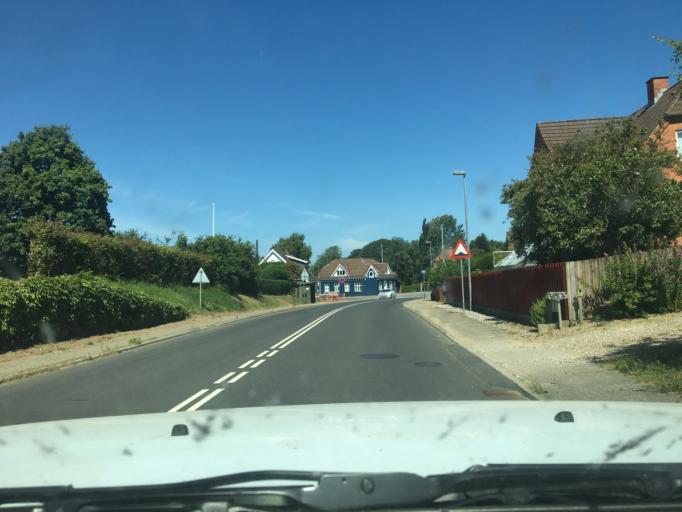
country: DK
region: Central Jutland
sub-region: Favrskov Kommune
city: Ulstrup
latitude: 56.4098
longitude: 9.7905
